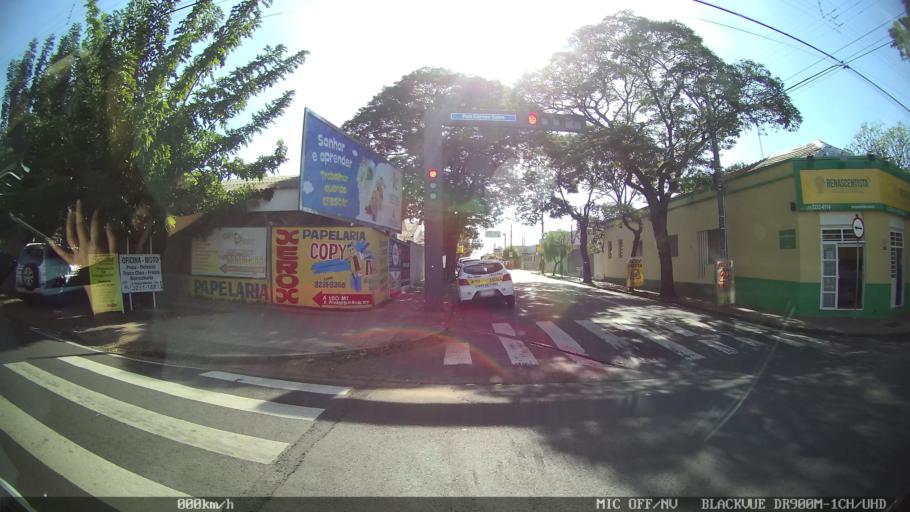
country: BR
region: Sao Paulo
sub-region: Sao Jose Do Rio Preto
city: Sao Jose do Rio Preto
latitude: -20.8005
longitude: -49.3868
